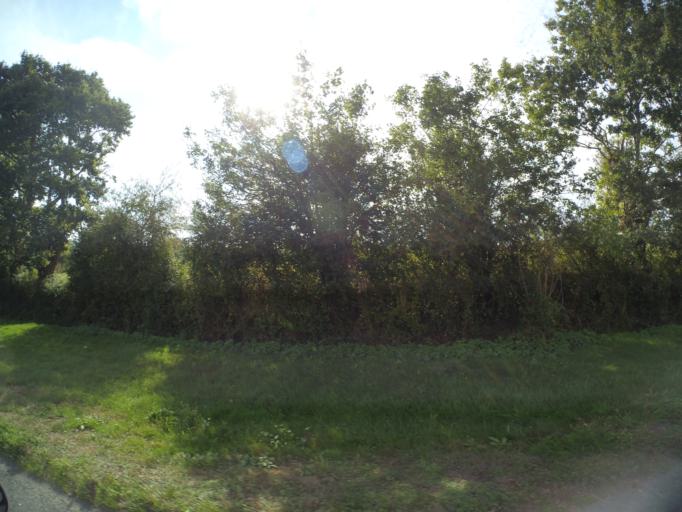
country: FR
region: Pays de la Loire
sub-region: Departement de Maine-et-Loire
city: La Chapelle-du-Genet
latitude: 47.1861
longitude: -1.0366
